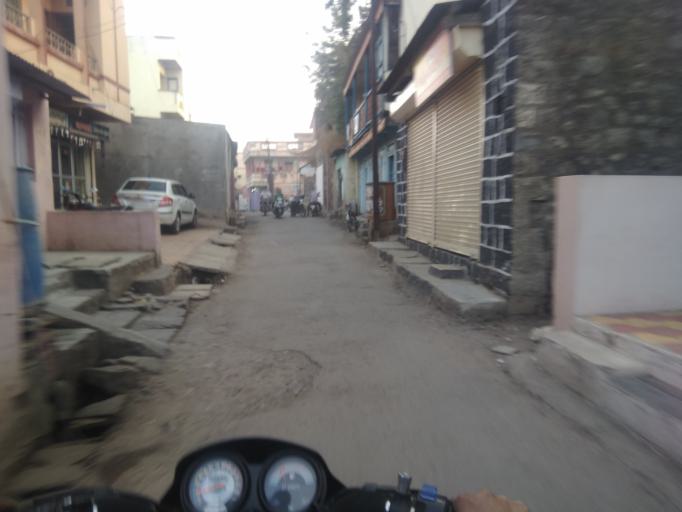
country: IN
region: Maharashtra
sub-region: Solapur
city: Sangola
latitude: 17.4372
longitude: 75.1931
